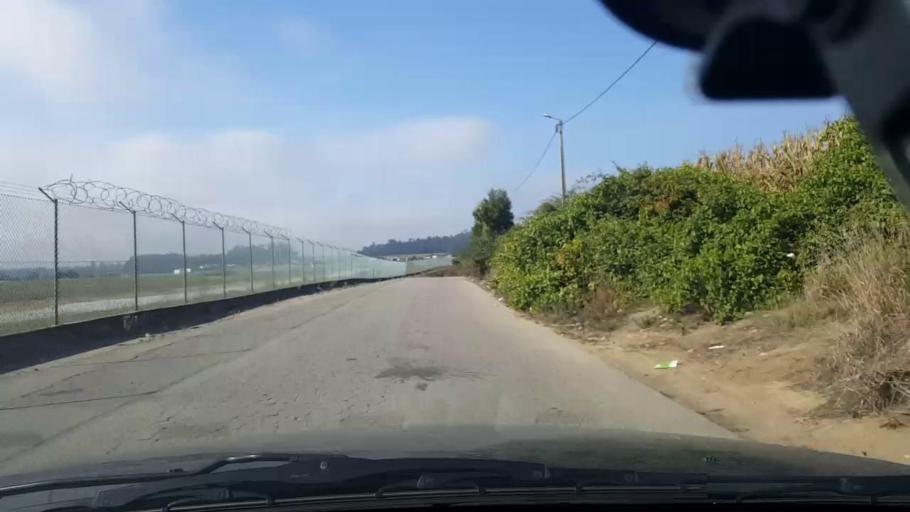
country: PT
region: Porto
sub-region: Matosinhos
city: Lavra
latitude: 41.2641
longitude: -8.6832
